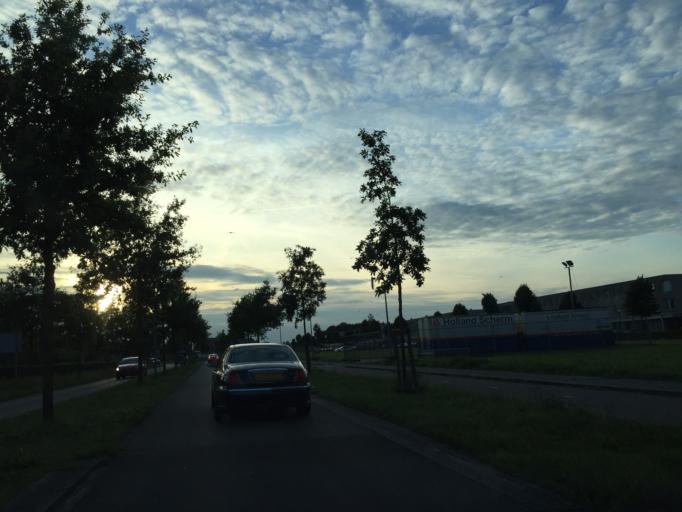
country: NL
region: South Holland
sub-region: Gemeente Rijnwoude
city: Benthuizen
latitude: 52.0658
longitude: 4.5341
